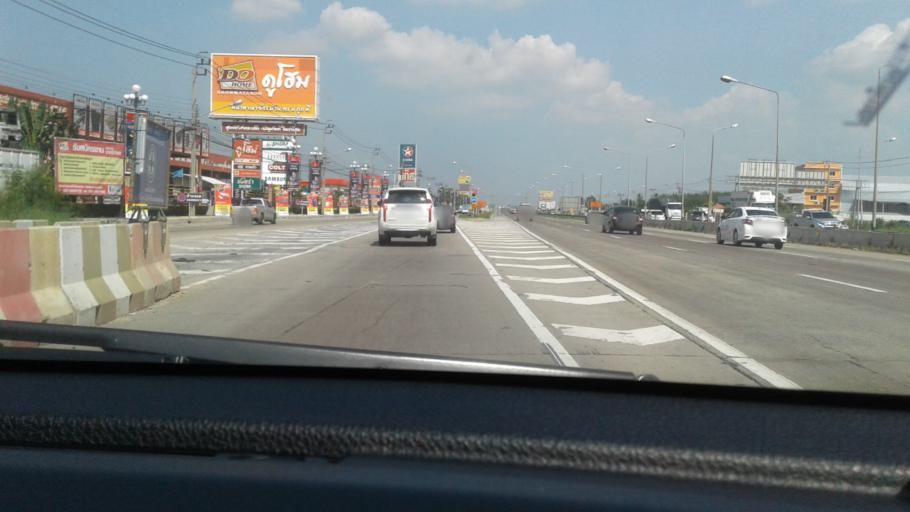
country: TH
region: Nonthaburi
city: Bang Bua Thong
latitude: 13.9481
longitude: 100.4220
